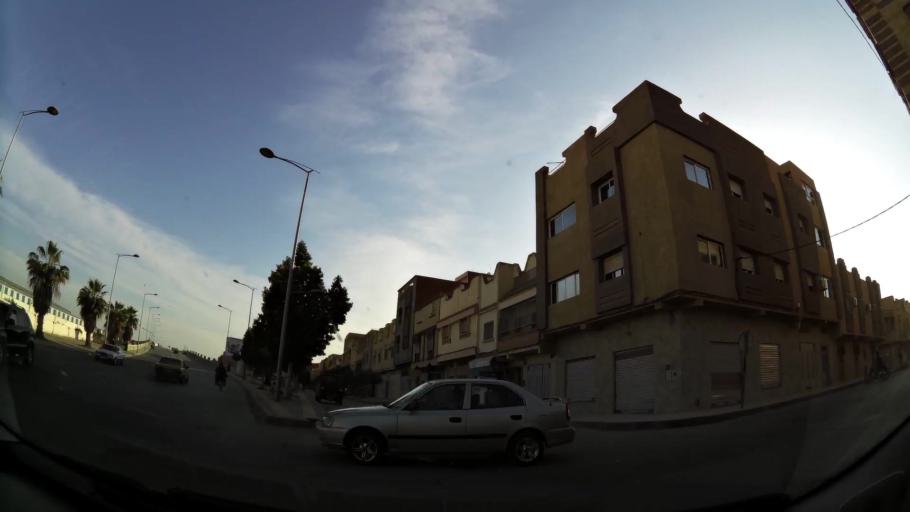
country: MA
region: Oriental
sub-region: Oujda-Angad
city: Oujda
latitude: 34.7044
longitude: -1.8956
